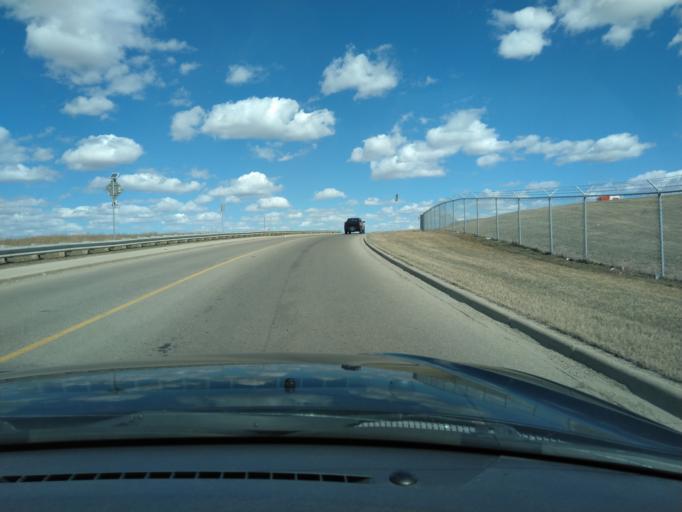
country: CA
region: Alberta
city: Calgary
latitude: 51.1270
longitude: -114.0423
